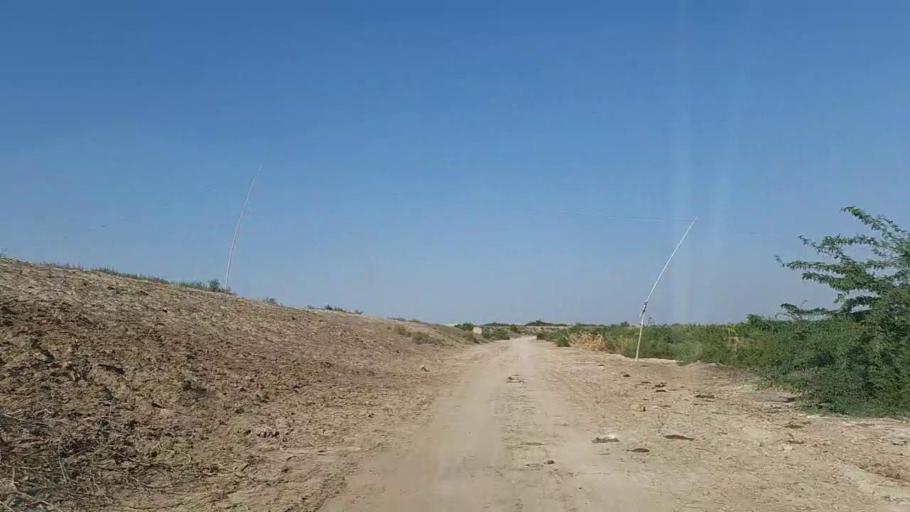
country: PK
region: Sindh
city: Chuhar Jamali
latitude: 24.5775
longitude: 68.0296
